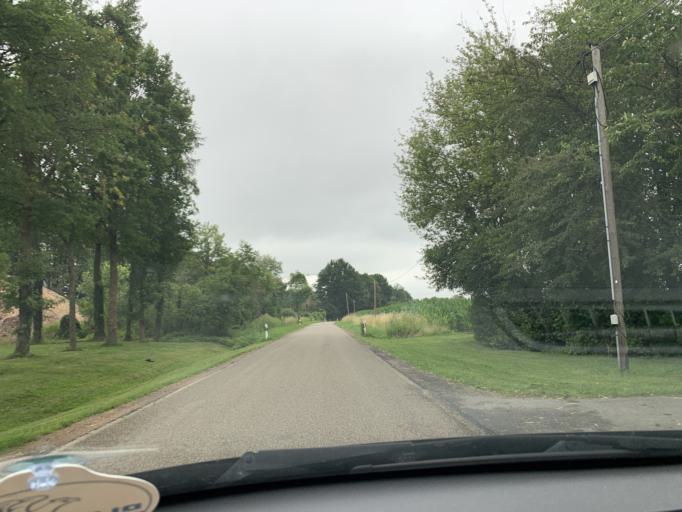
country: DE
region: North Rhine-Westphalia
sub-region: Regierungsbezirk Munster
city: Havixbeck
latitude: 52.0187
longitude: 7.4224
